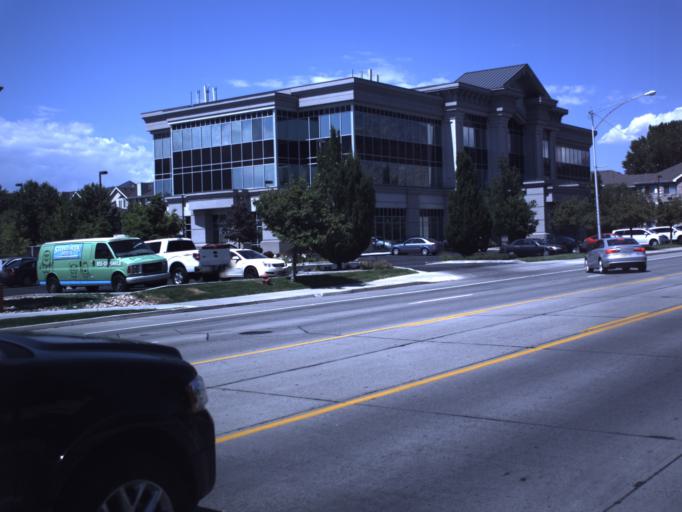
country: US
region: Utah
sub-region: Utah County
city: Provo
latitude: 40.2516
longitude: -111.6585
